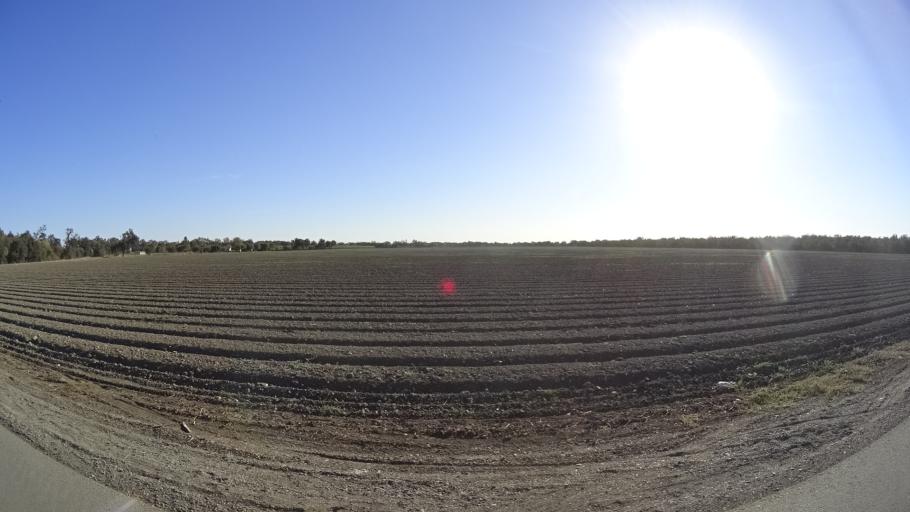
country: US
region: California
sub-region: Yolo County
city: Davis
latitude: 38.6032
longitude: -121.7855
